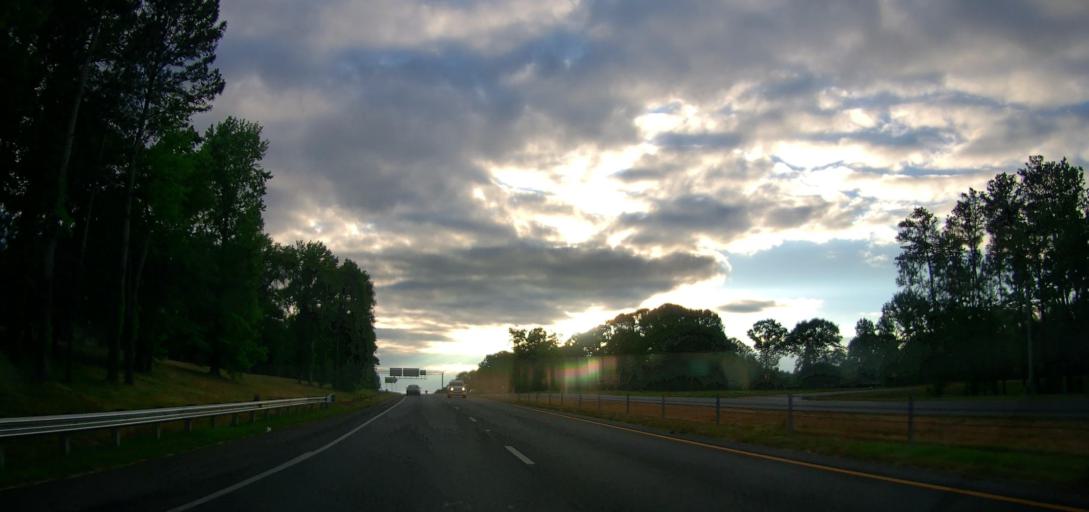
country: US
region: Georgia
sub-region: Clarke County
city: Athens
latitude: 33.9784
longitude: -83.3641
